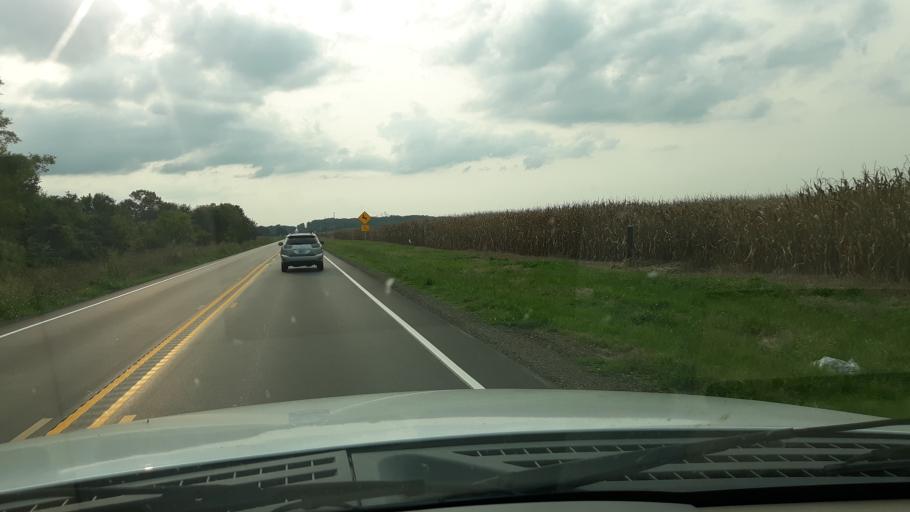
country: US
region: Indiana
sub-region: Gibson County
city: Princeton
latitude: 38.3558
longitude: -87.6284
